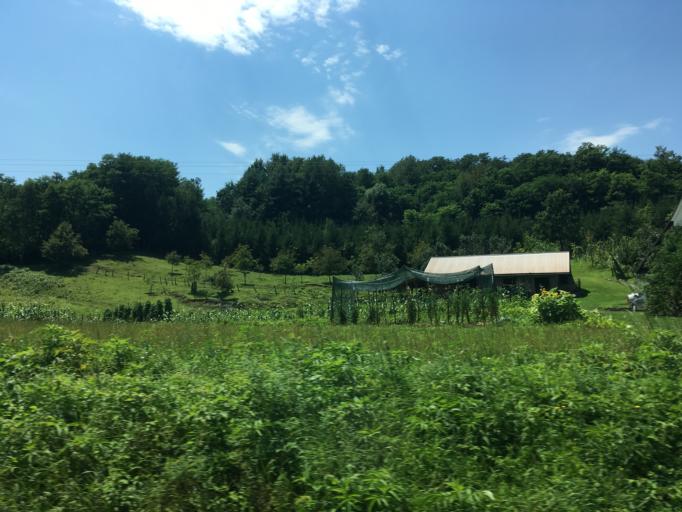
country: SI
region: Metlika
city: Metlika
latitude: 45.6048
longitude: 15.3323
